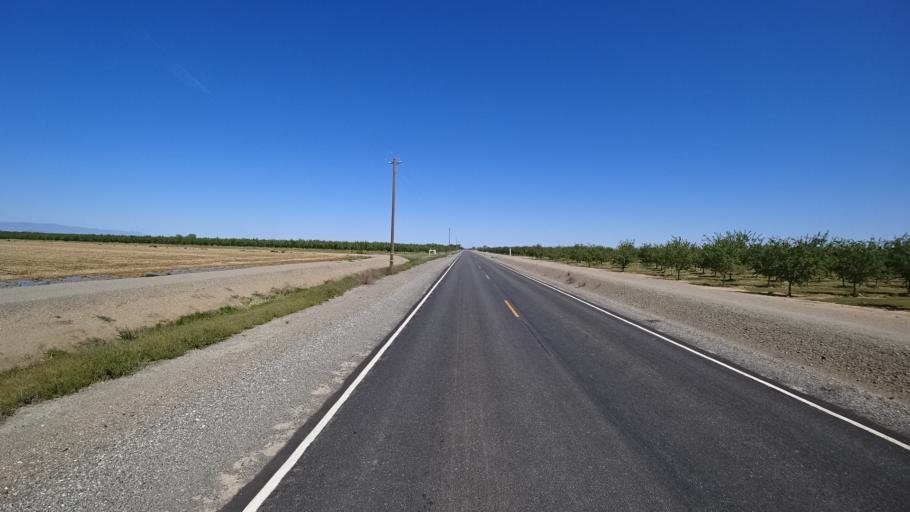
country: US
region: California
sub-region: Glenn County
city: Orland
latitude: 39.6589
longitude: -122.1408
